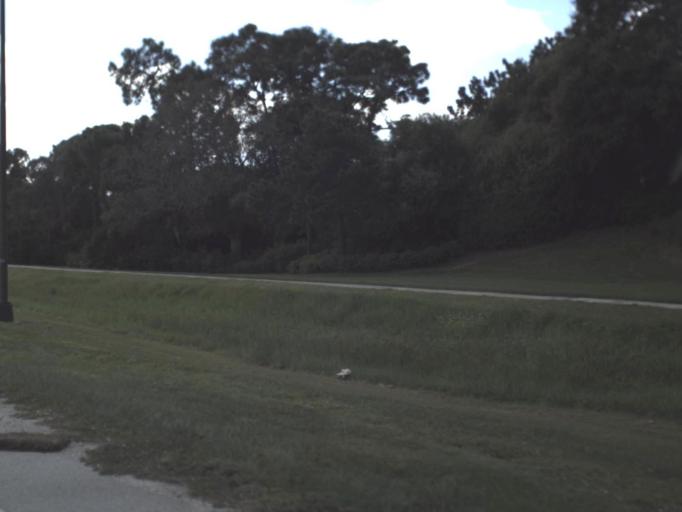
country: US
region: Florida
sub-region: Lee County
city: Bonita Springs
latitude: 26.3647
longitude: -81.8079
